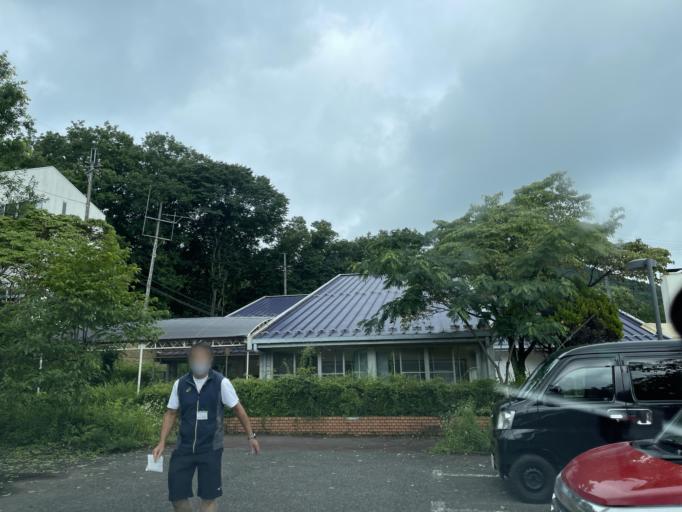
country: JP
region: Saitama
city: Hanno
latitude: 35.8600
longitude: 139.2685
